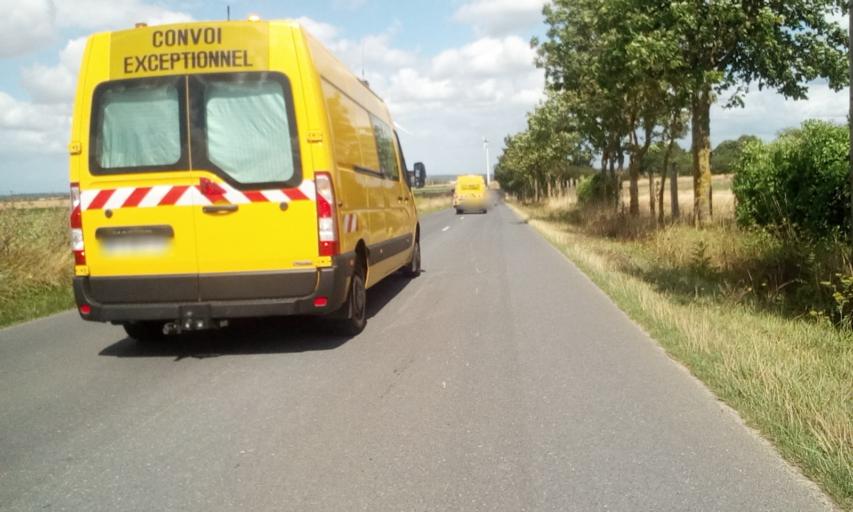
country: FR
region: Lower Normandy
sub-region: Departement du Calvados
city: Cagny
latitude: 49.1134
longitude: -0.2617
